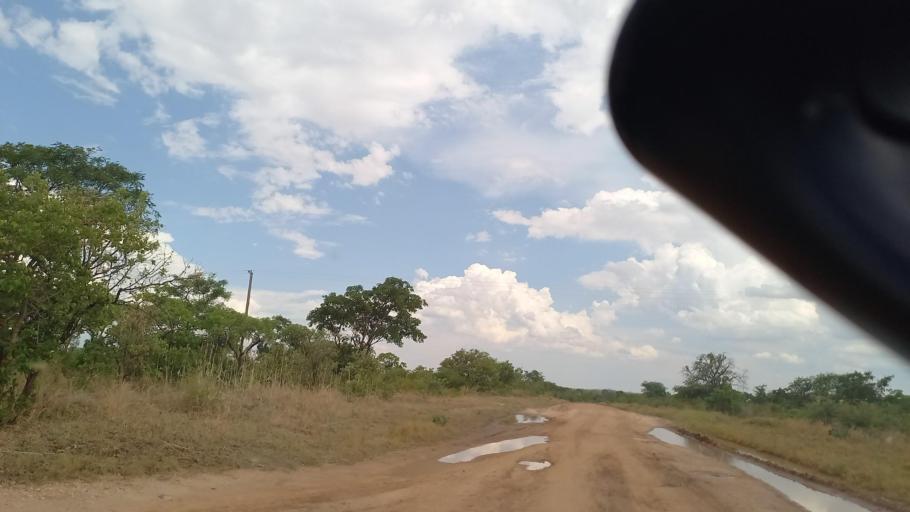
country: ZM
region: Southern
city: Nakambala
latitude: -16.0610
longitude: 27.9925
